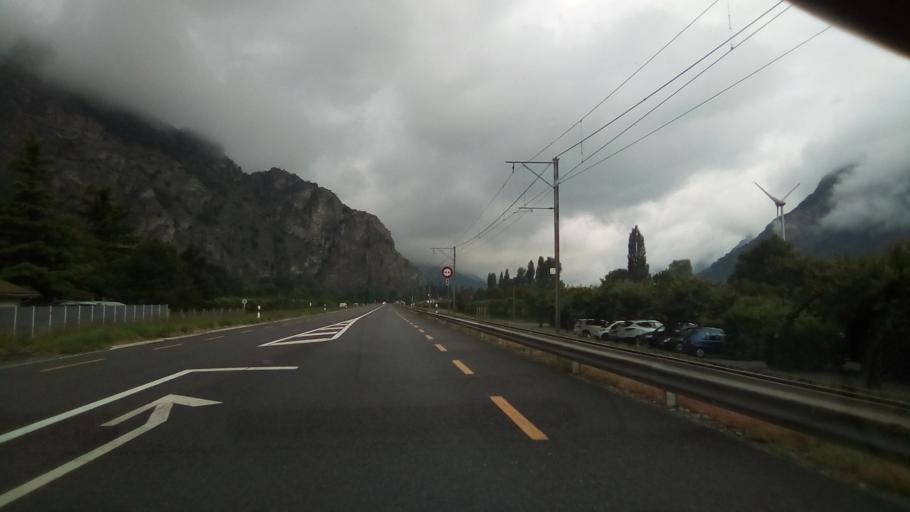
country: CH
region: Valais
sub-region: Saint-Maurice District
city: Vernayaz
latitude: 46.1199
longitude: 7.0529
